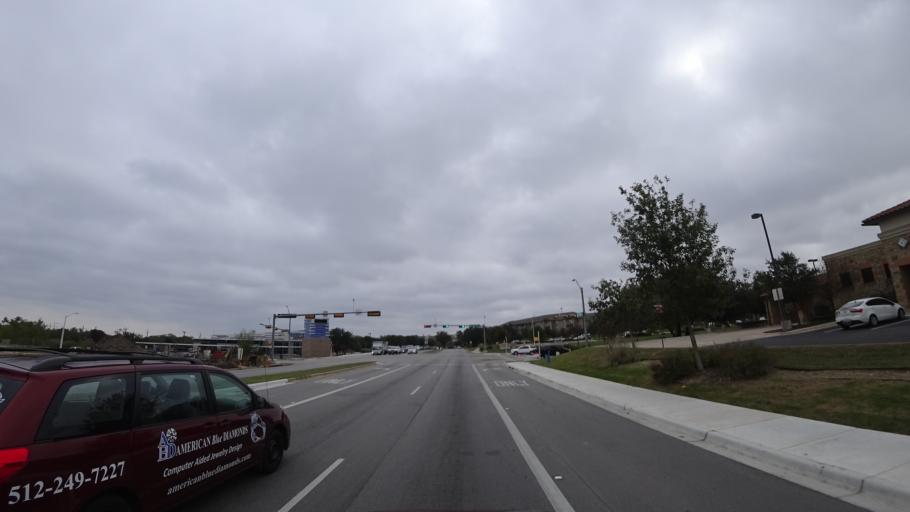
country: US
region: Texas
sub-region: Williamson County
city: Cedar Park
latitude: 30.4810
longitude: -97.8290
